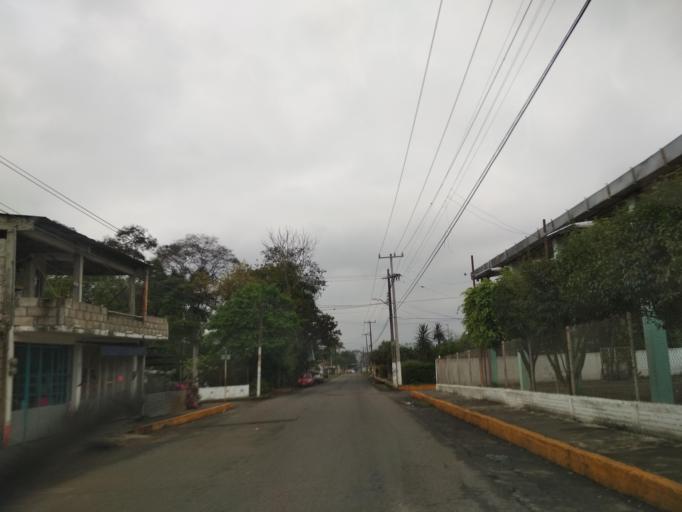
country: MX
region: Veracruz
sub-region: Cordoba
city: Veinte de Noviembre
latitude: 18.8641
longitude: -96.9541
